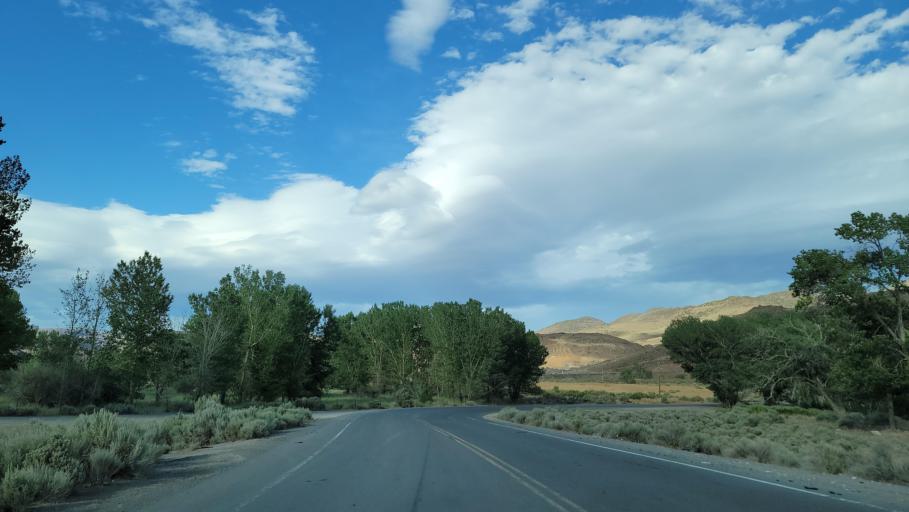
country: US
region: Nevada
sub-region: Washoe County
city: Sparks
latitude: 39.5186
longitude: -119.6176
